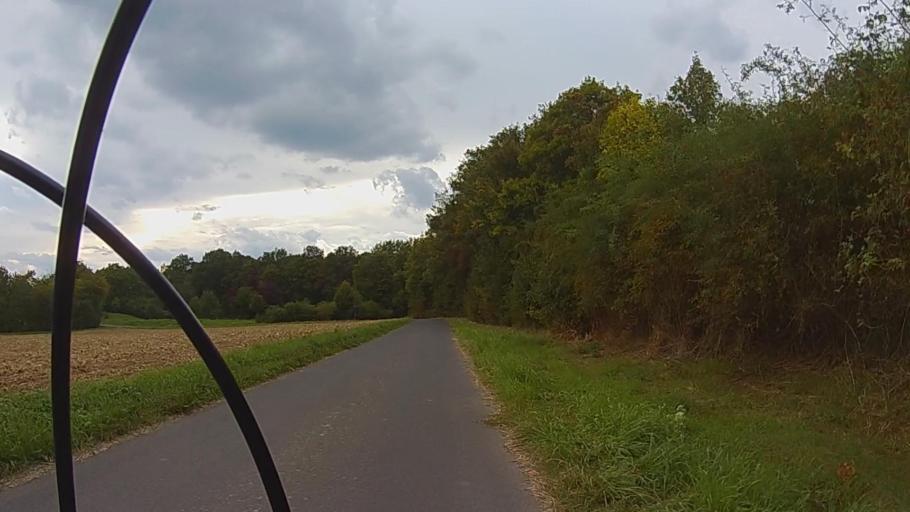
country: DE
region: Hesse
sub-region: Regierungsbezirk Darmstadt
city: Oberursel
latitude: 50.2031
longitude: 8.6041
